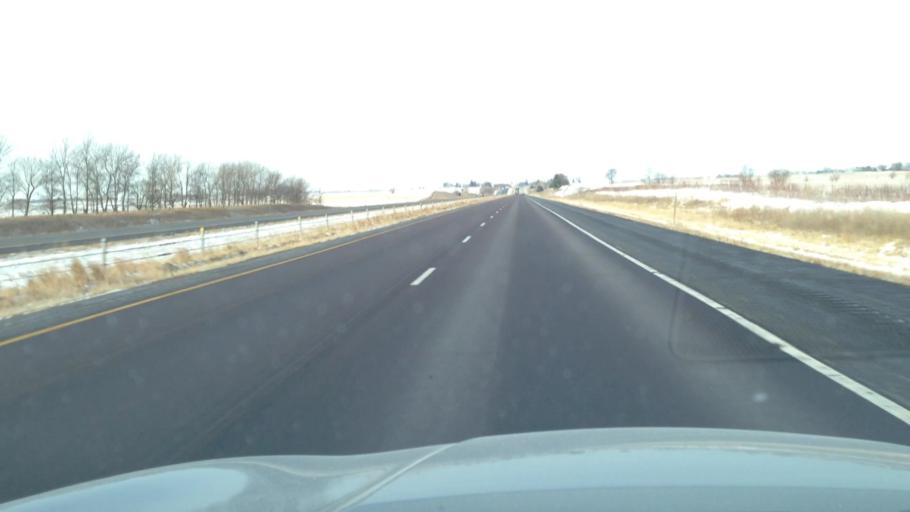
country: US
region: Iowa
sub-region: Poweshiek County
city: Grinnell
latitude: 41.6956
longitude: -92.6744
